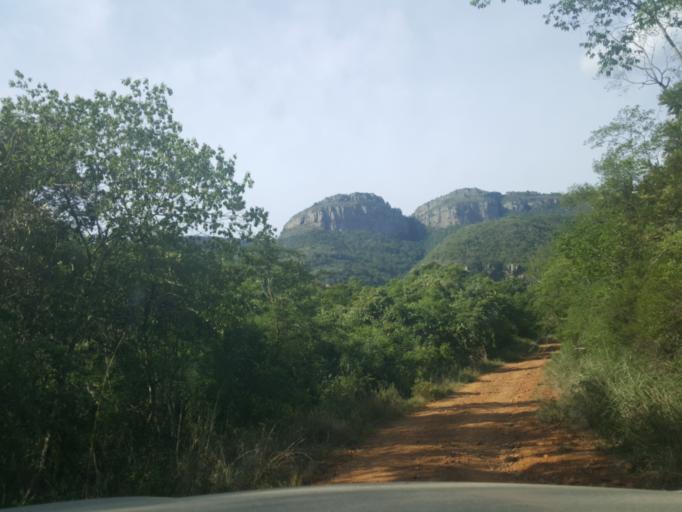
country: ZA
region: Limpopo
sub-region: Mopani District Municipality
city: Hoedspruit
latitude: -24.5937
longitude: 30.8276
